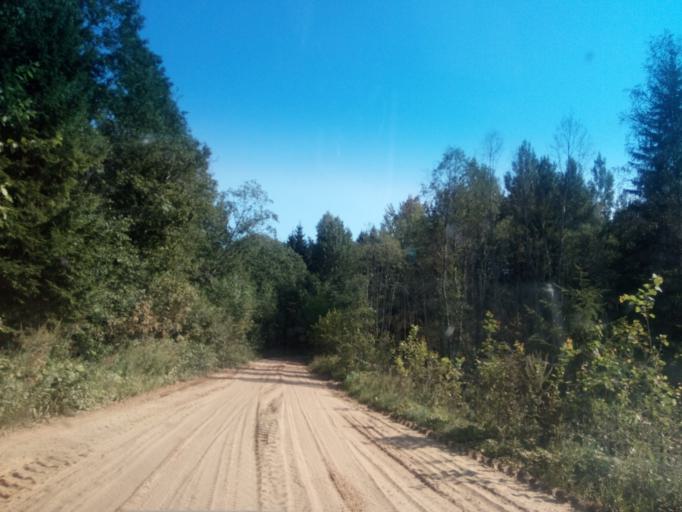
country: BY
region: Vitebsk
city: Dzisna
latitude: 55.6502
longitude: 28.3190
